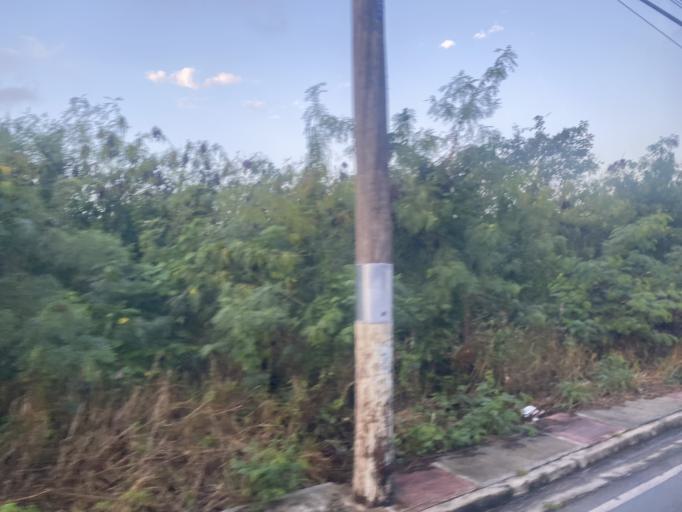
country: DO
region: San Juan
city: Punta Cana
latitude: 18.7118
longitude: -68.4649
